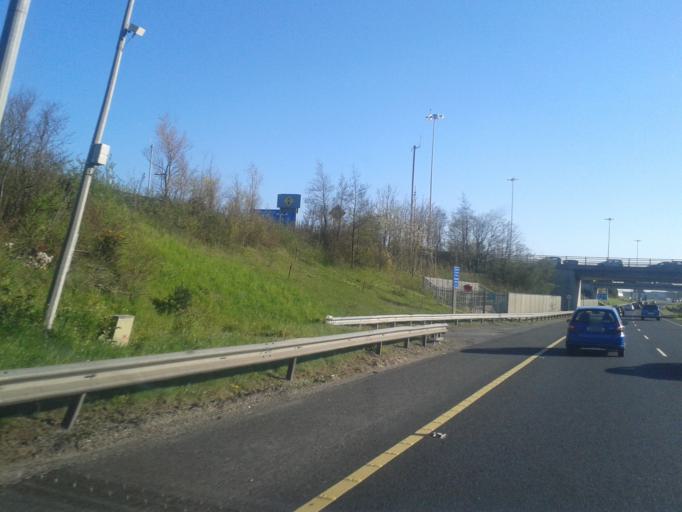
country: IE
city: Bonnybrook
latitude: 53.4119
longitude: -6.2255
